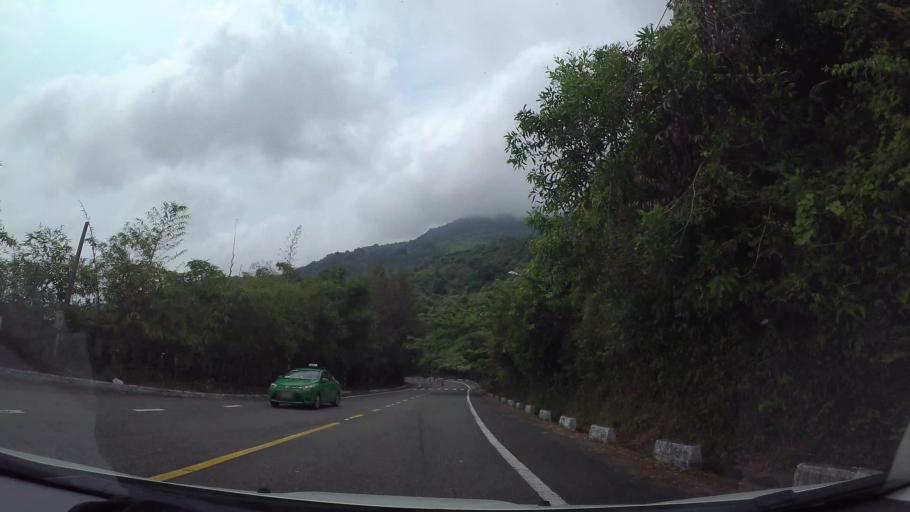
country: VN
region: Da Nang
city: Son Tra
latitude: 16.1063
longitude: 108.2959
